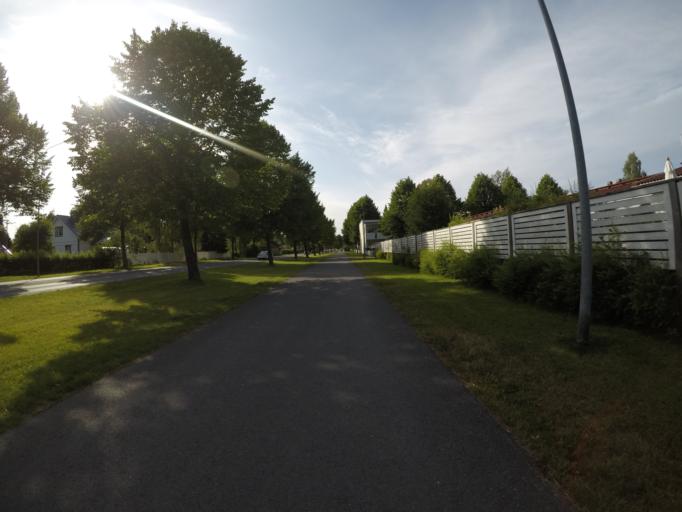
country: FI
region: Haeme
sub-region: Haemeenlinna
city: Haemeenlinna
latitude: 60.9813
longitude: 24.4204
